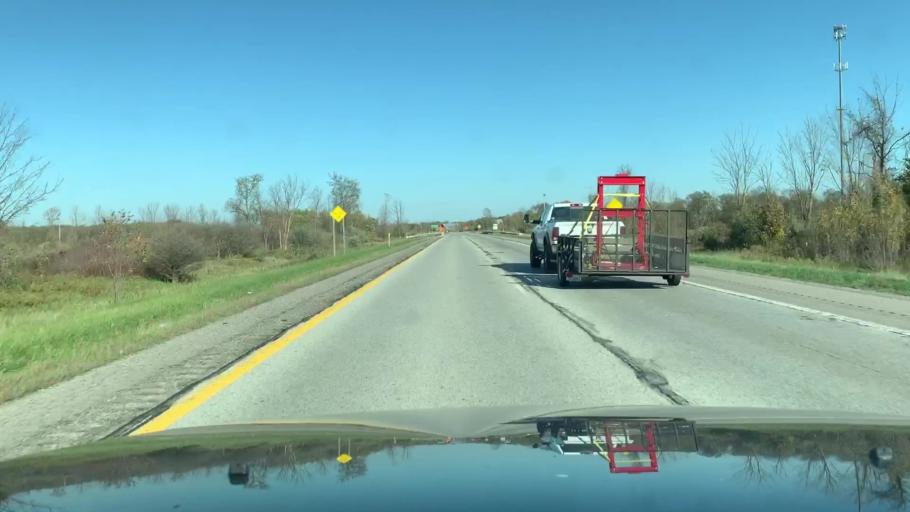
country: US
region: Michigan
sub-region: Ottawa County
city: Hudsonville
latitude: 42.8346
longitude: -85.9032
